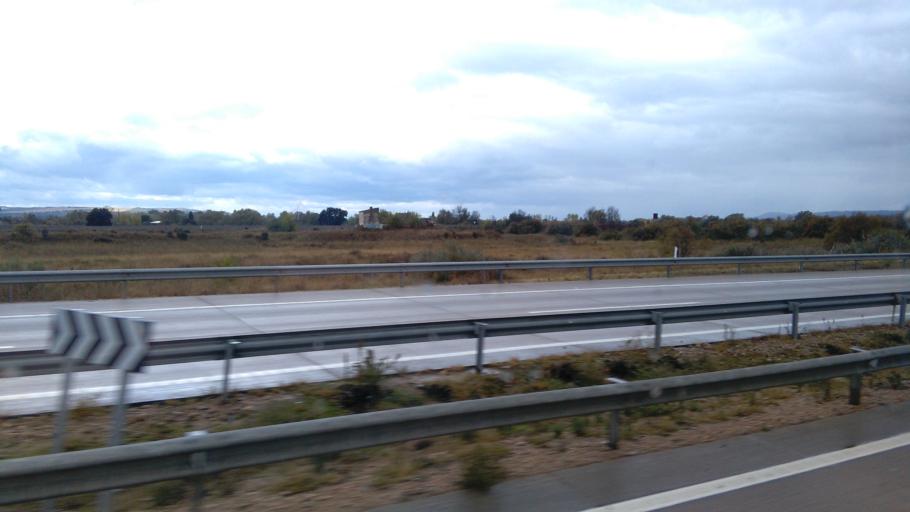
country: ES
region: Castille-La Mancha
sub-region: Province of Toledo
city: Cazalegas
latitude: 39.9827
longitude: -4.7519
